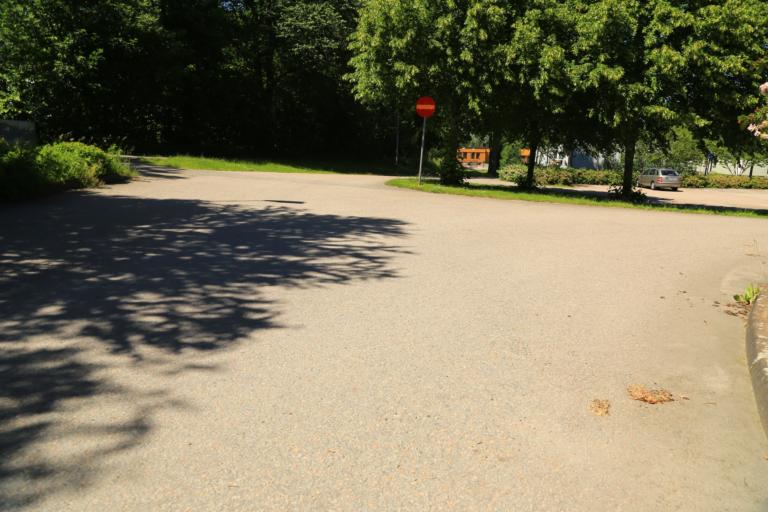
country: SE
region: Halland
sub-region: Varbergs Kommun
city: Varberg
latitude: 57.1029
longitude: 12.2835
